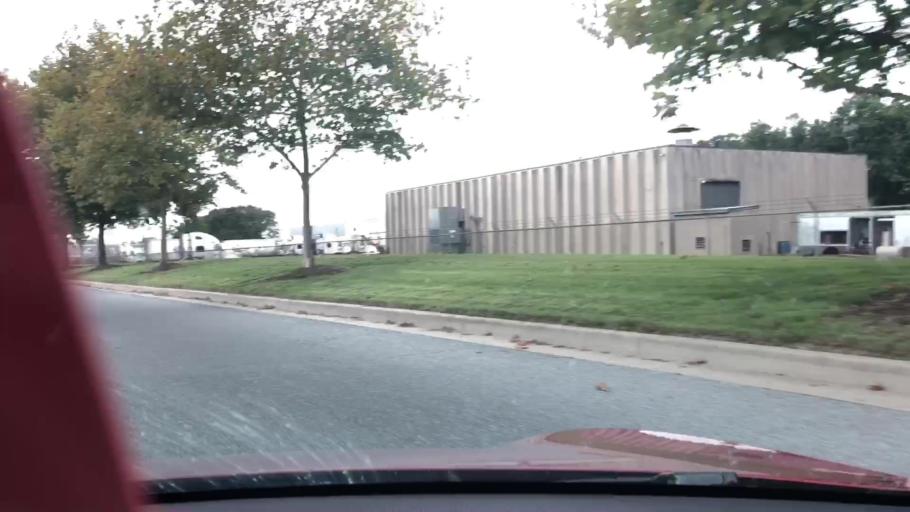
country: US
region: Maryland
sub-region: Wicomico County
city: Salisbury
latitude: 38.4018
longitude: -75.5652
